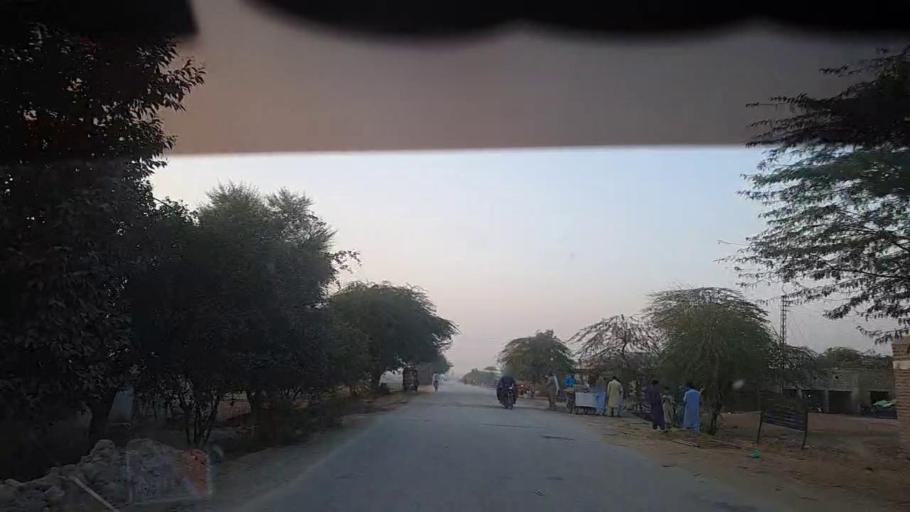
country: PK
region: Sindh
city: Ranipur
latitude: 27.2668
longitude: 68.5208
